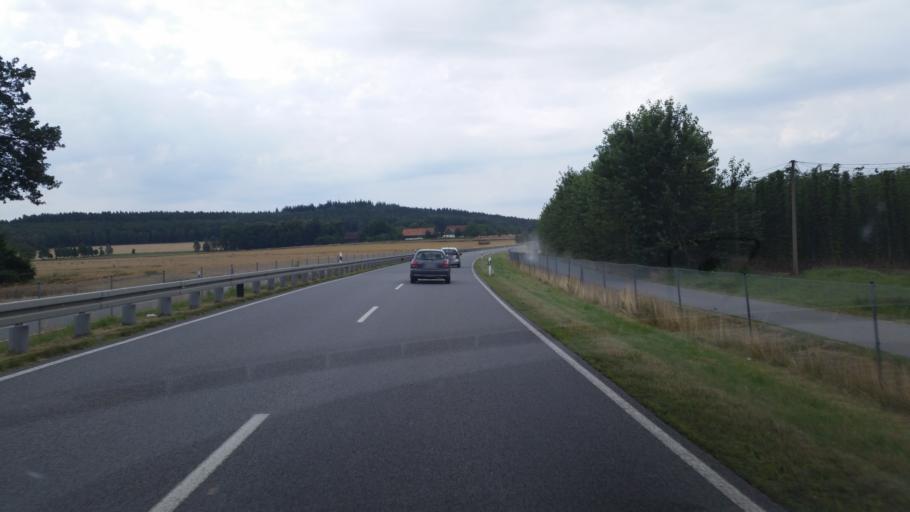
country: DE
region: Saxony
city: Elstra
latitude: 51.2166
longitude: 14.1536
